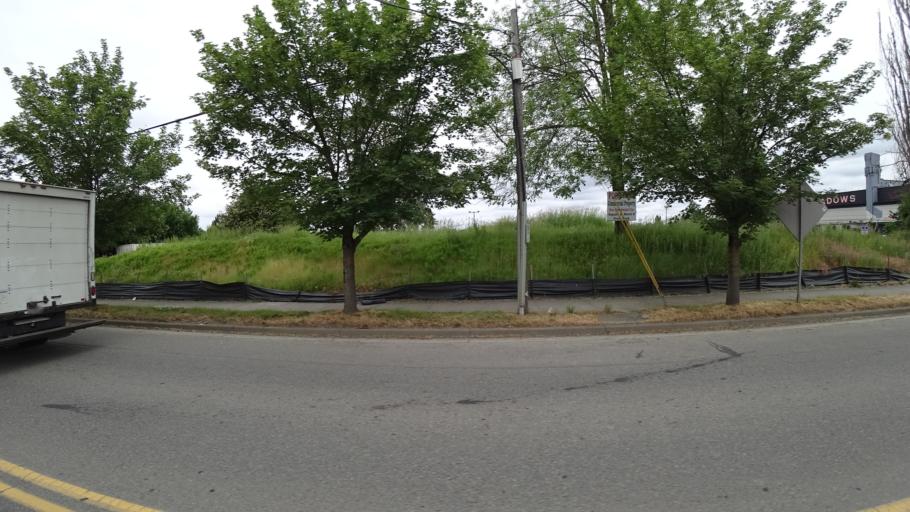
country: US
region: Washington
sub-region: Clark County
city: Vancouver
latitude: 45.5895
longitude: -122.6786
